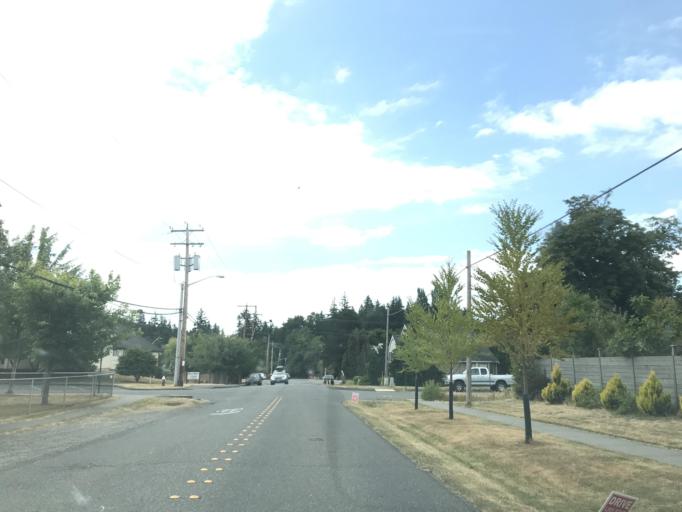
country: US
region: Washington
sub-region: Whatcom County
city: Bellingham
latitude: 48.7189
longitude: -122.4998
